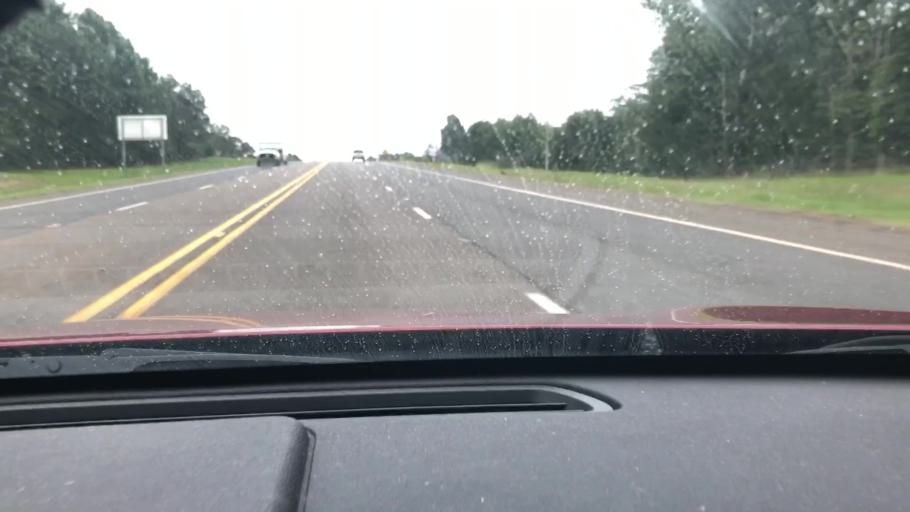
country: US
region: Arkansas
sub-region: Lafayette County
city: Lewisville
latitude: 33.3574
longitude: -93.5595
